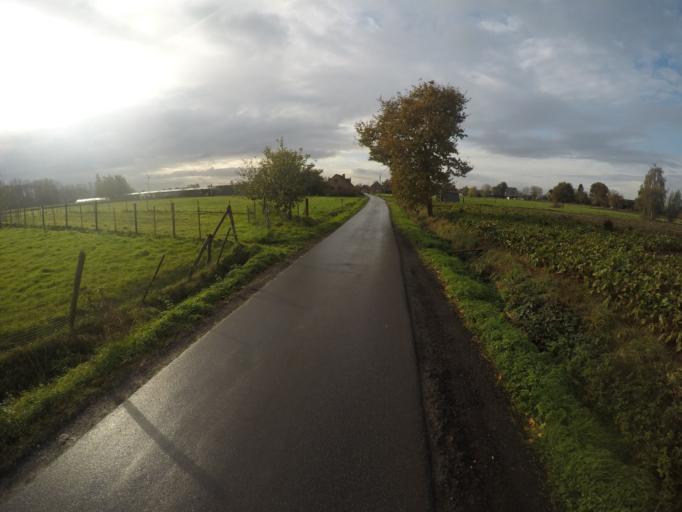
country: BE
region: Flanders
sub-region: Provincie Antwerpen
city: Zwijndrecht
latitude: 51.2082
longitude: 4.3026
